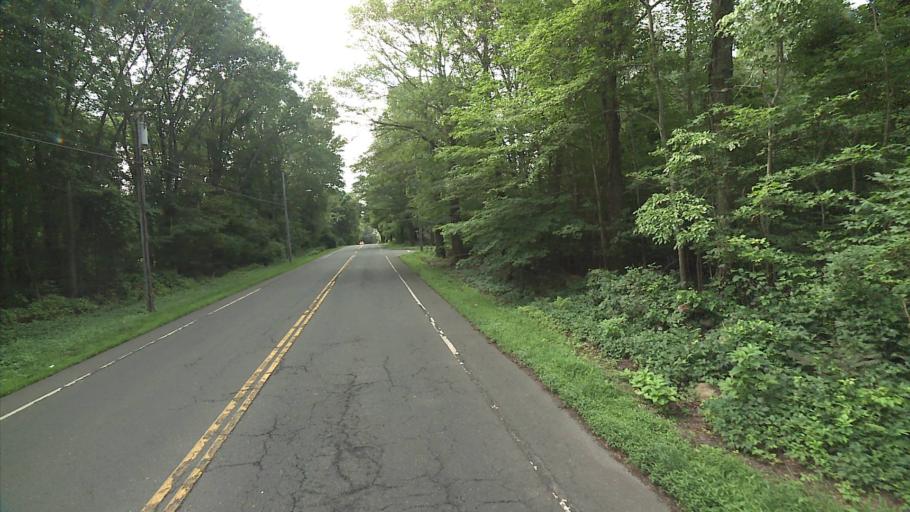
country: US
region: Connecticut
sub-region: Middlesex County
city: Clinton
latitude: 41.3334
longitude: -72.4930
